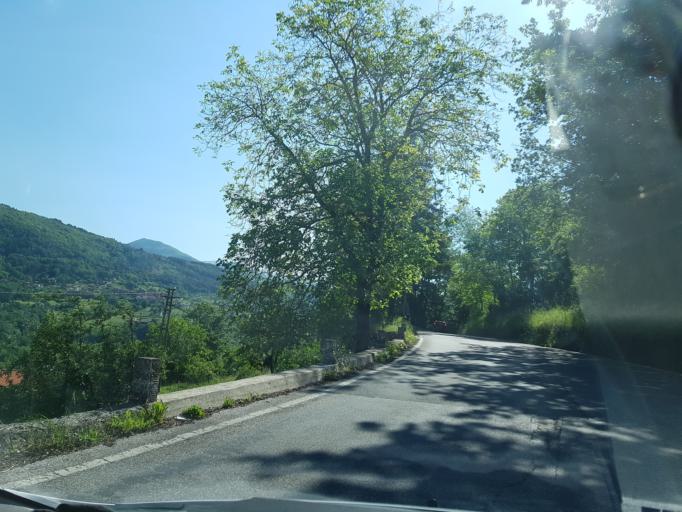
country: IT
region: Tuscany
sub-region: Provincia di Lucca
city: Camporgiano
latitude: 44.1550
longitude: 10.3379
